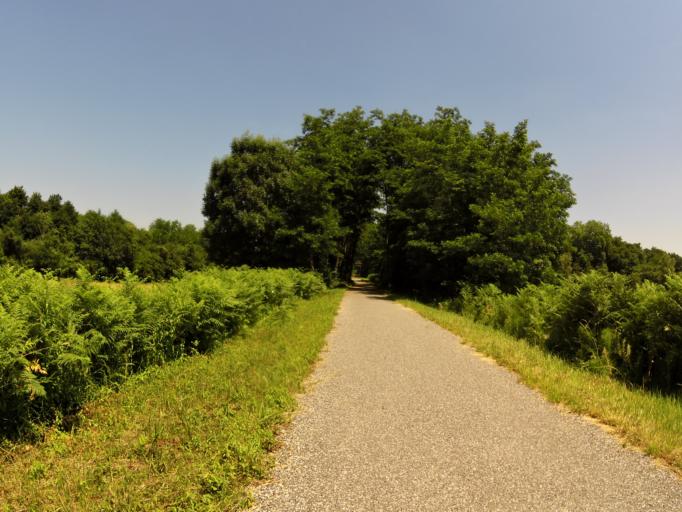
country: FR
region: Aquitaine
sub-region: Departement des Pyrenees-Atlantiques
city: Salies-de-Bearn
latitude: 43.4611
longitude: -0.9809
